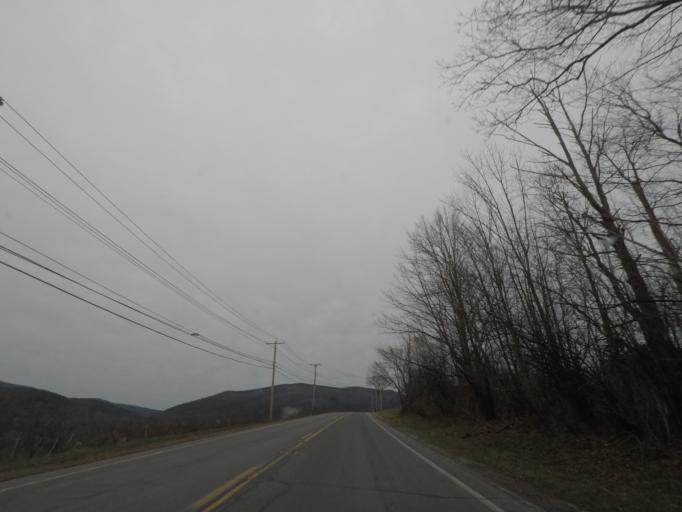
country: US
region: Massachusetts
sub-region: Berkshire County
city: Williamstown
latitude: 42.6677
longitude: -73.2387
